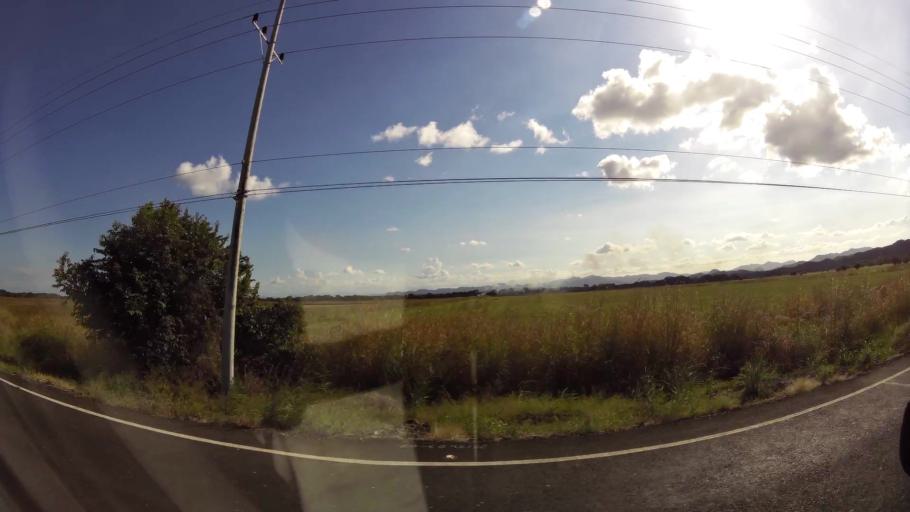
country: CR
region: Guanacaste
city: Sardinal
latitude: 10.5662
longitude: -85.6136
